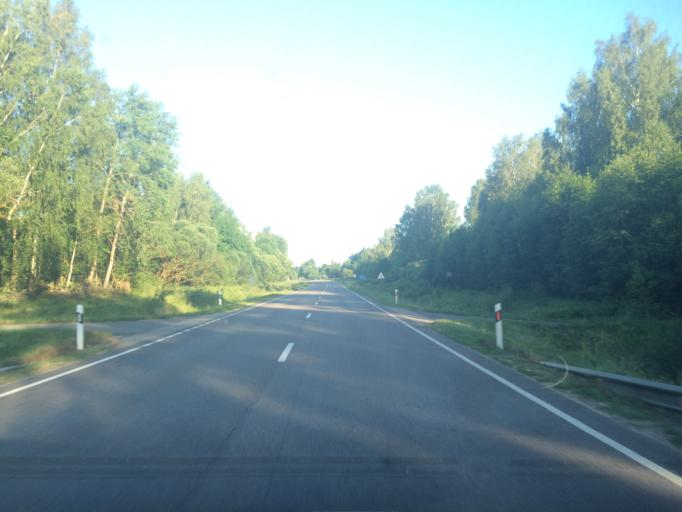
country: LT
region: Utenos apskritis
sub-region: Anyksciai
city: Anyksciai
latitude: 55.4056
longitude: 25.1157
